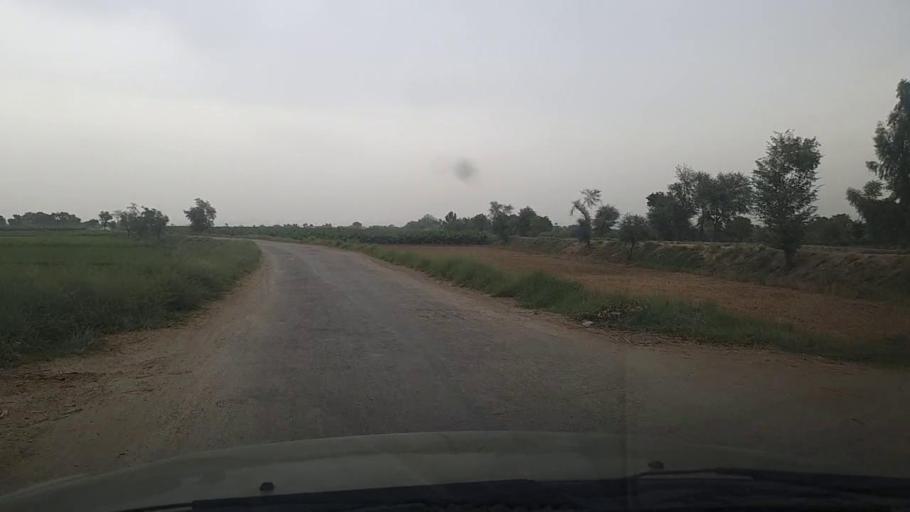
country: PK
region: Sindh
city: Daur
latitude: 26.3853
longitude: 68.1823
